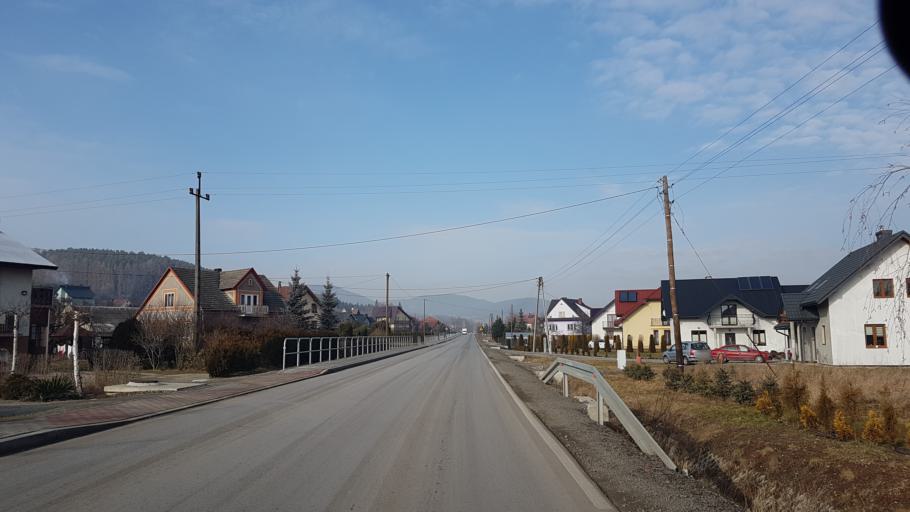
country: PL
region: Lesser Poland Voivodeship
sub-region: Powiat nowosadecki
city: Olszana
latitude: 49.5967
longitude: 20.5286
